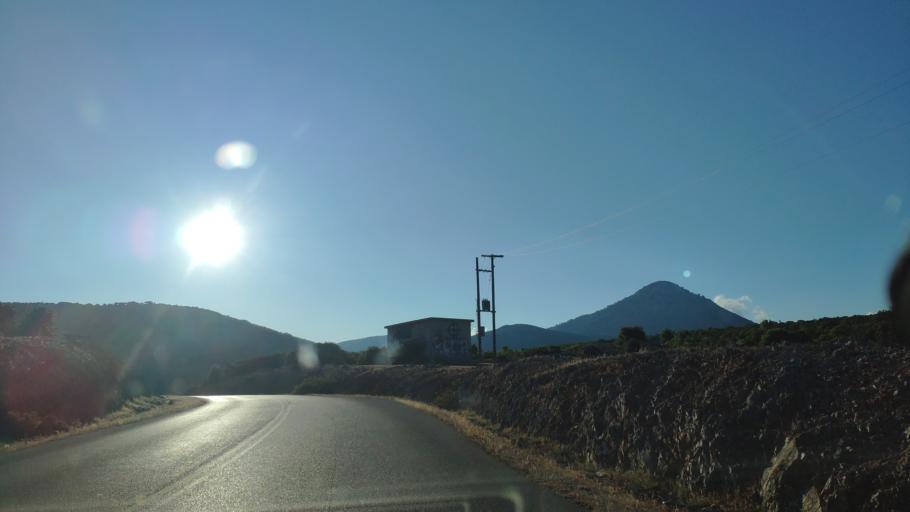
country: GR
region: West Greece
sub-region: Nomos Aitolias kai Akarnanias
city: Astakos
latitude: 38.6091
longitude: 21.1267
